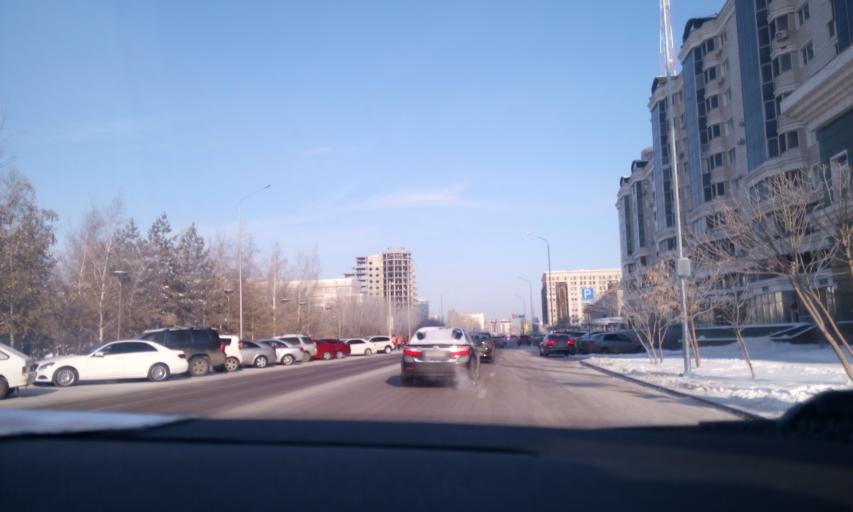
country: KZ
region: Astana Qalasy
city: Astana
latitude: 51.1285
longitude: 71.4326
